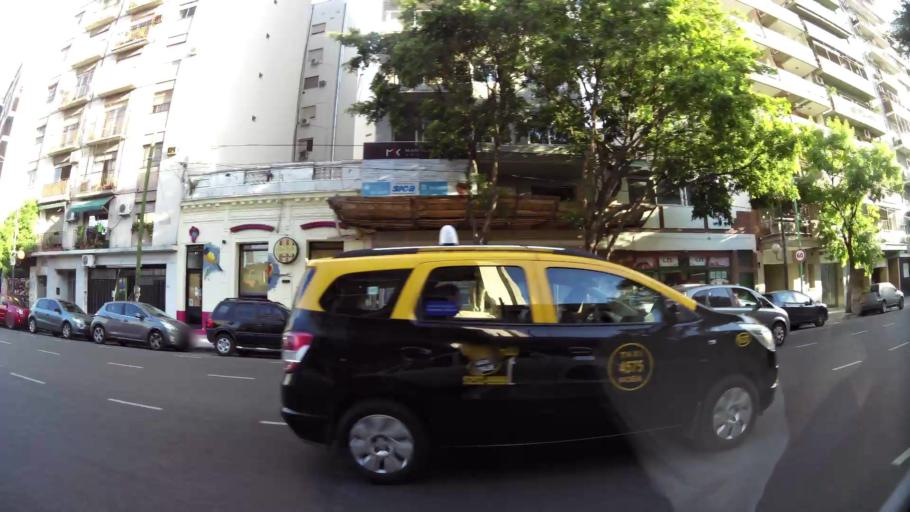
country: AR
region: Buenos Aires F.D.
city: Colegiales
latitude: -34.5979
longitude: -58.4270
